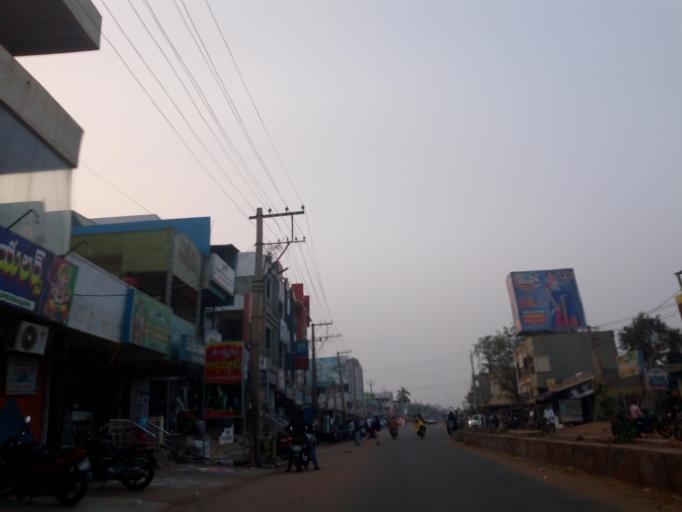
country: IN
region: Andhra Pradesh
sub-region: West Godavari
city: Eluru
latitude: 16.8217
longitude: 81.2633
